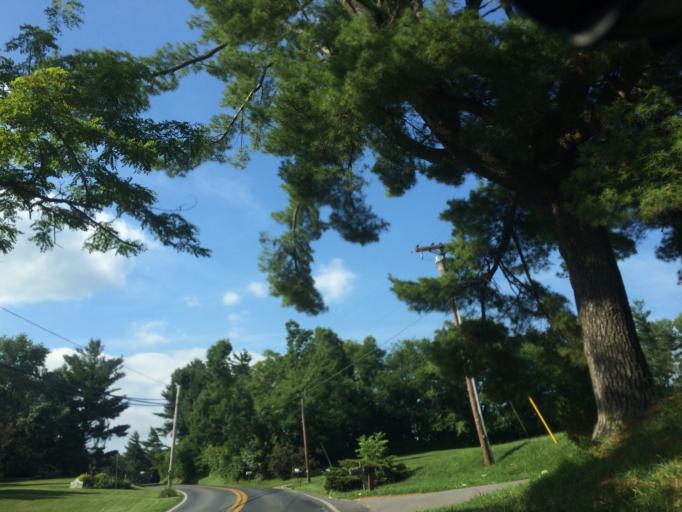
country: US
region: Maryland
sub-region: Carroll County
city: Sykesville
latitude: 39.3178
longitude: -77.0620
